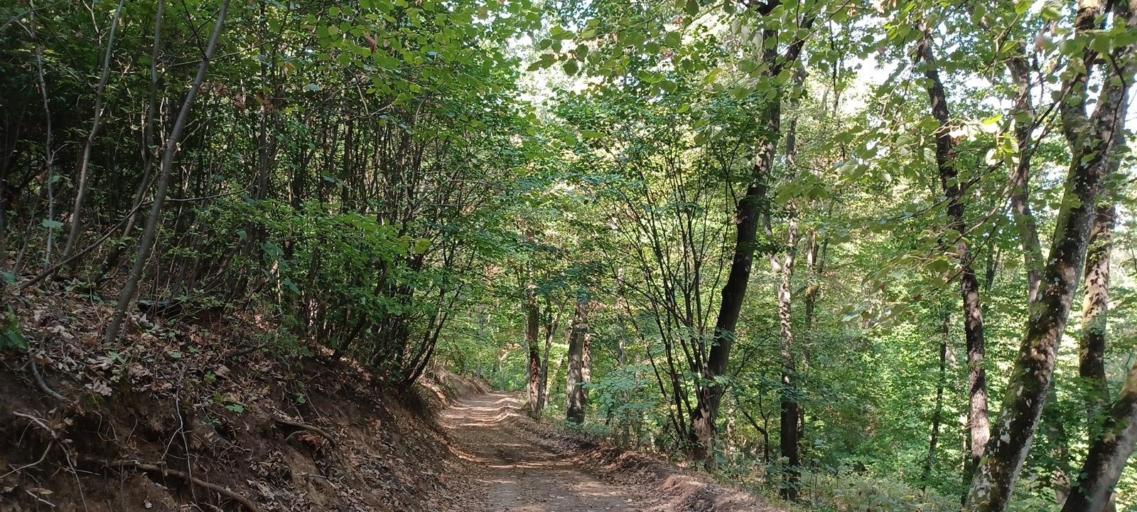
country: HU
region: Tolna
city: Szentgalpuszta
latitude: 46.3239
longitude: 18.6250
